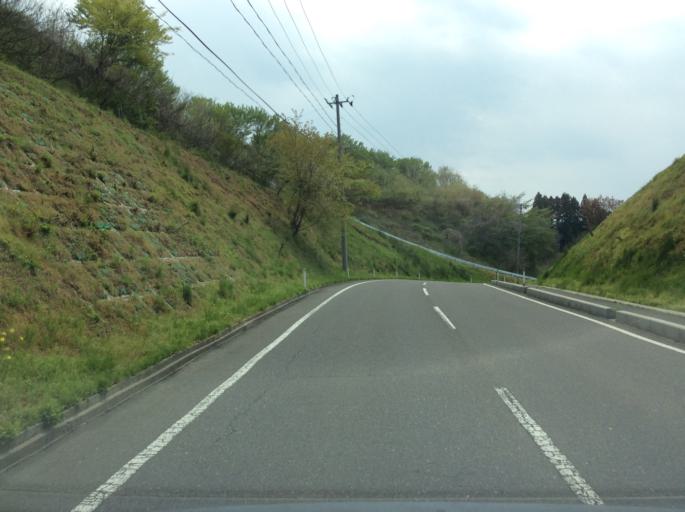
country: JP
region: Fukushima
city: Miharu
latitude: 37.3969
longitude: 140.4877
